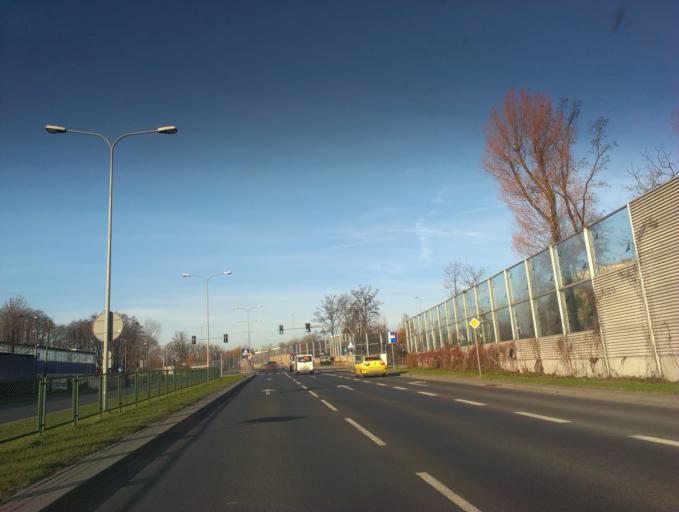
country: PL
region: Greater Poland Voivodeship
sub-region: Poznan
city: Poznan
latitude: 52.4371
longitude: 16.9538
